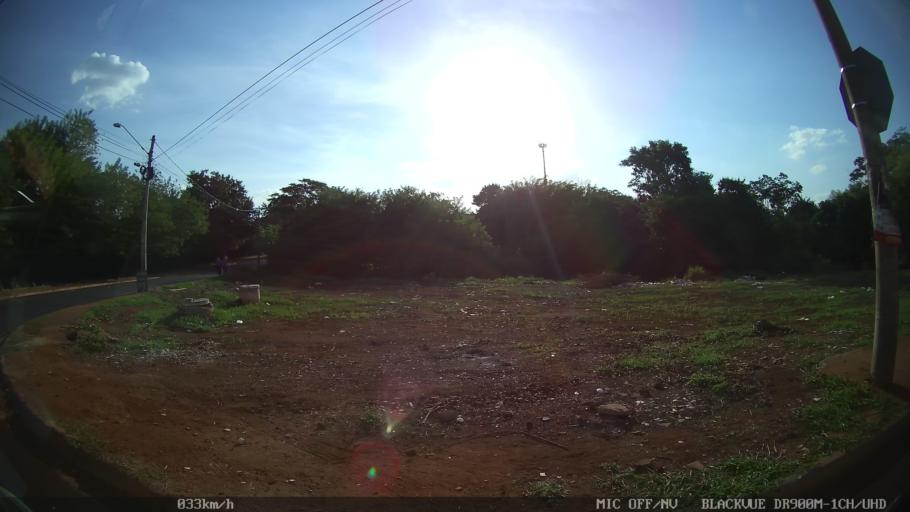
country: BR
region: Sao Paulo
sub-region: Ribeirao Preto
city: Ribeirao Preto
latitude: -21.1480
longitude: -47.8368
